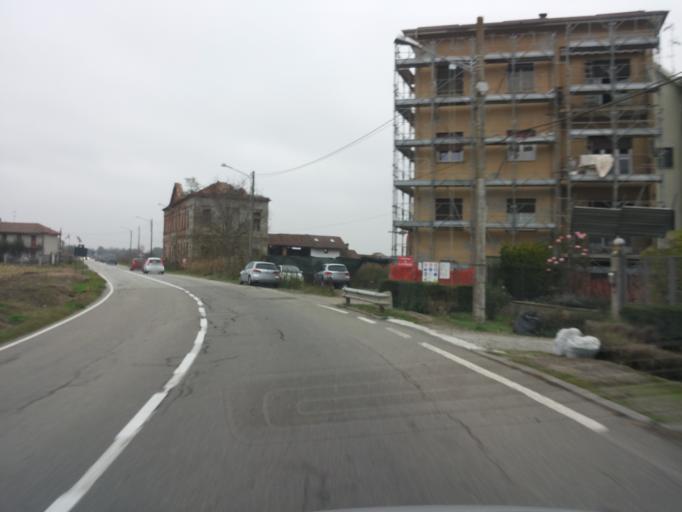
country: IT
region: Piedmont
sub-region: Provincia di Vercelli
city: Borgo Vercelli
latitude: 45.3593
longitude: 8.4721
